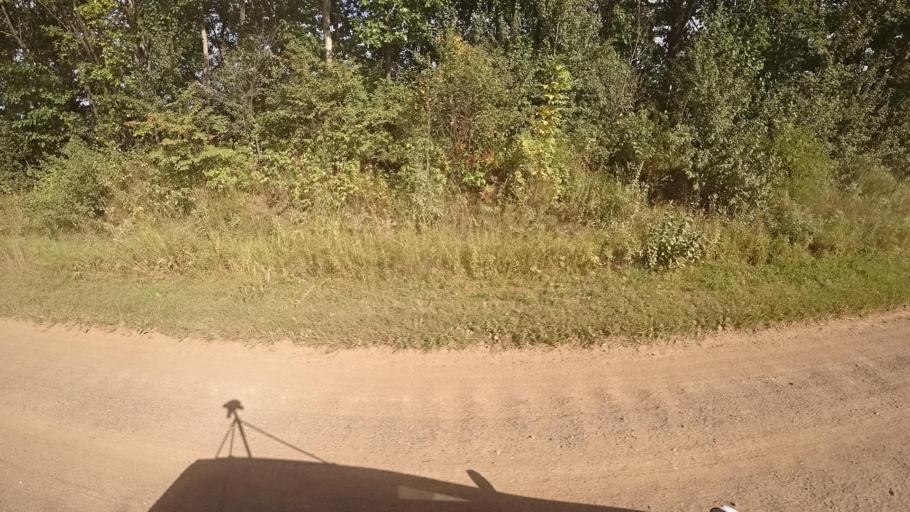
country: RU
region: Primorskiy
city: Yakovlevka
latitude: 44.4192
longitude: 133.5708
